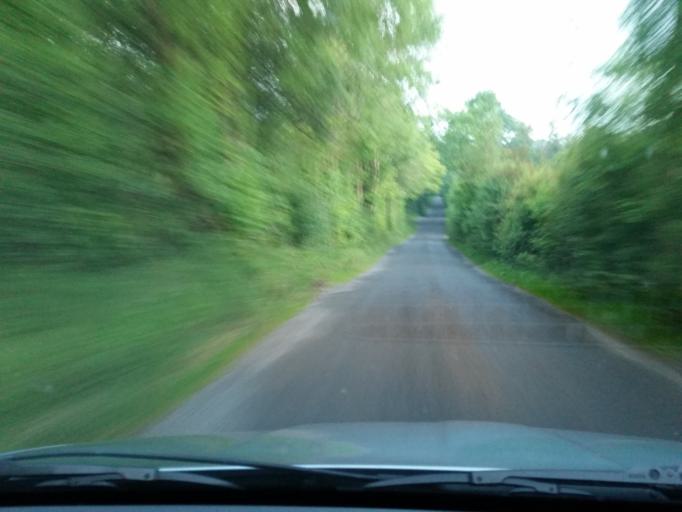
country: GB
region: Northern Ireland
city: Fivemiletown
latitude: 54.3053
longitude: -7.2943
